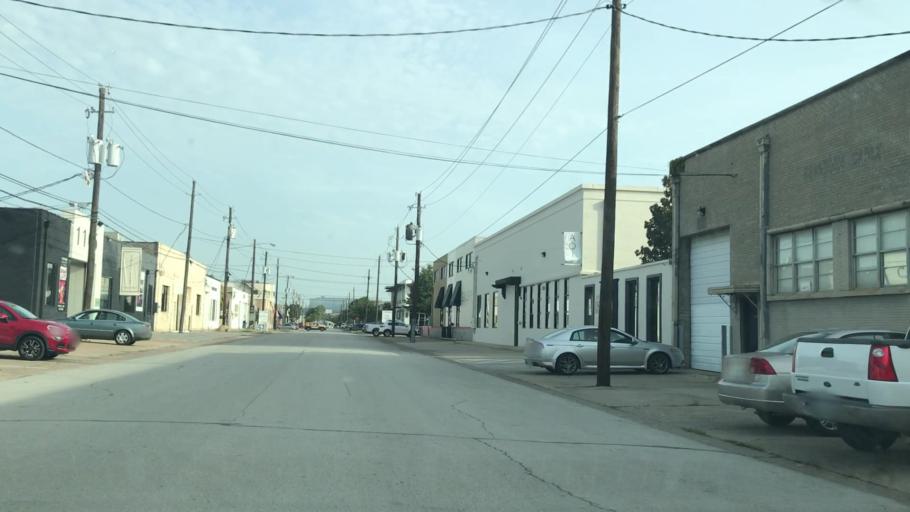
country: US
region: Texas
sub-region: Dallas County
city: Dallas
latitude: 32.7873
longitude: -96.8167
